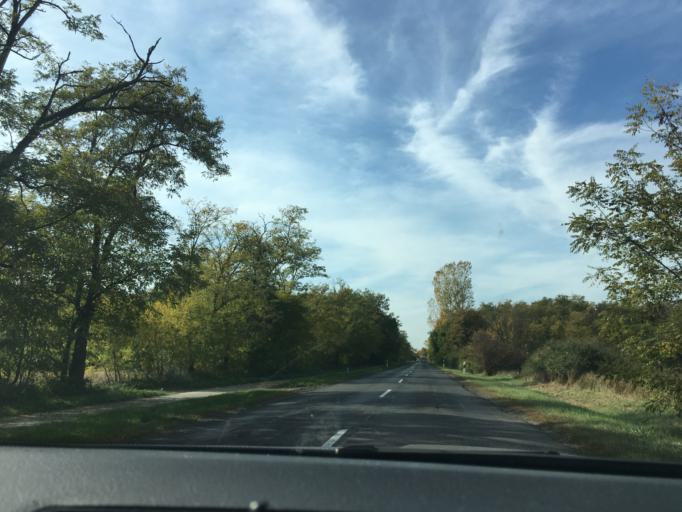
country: HU
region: Hajdu-Bihar
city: Vamospercs
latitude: 47.5265
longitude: 21.9328
